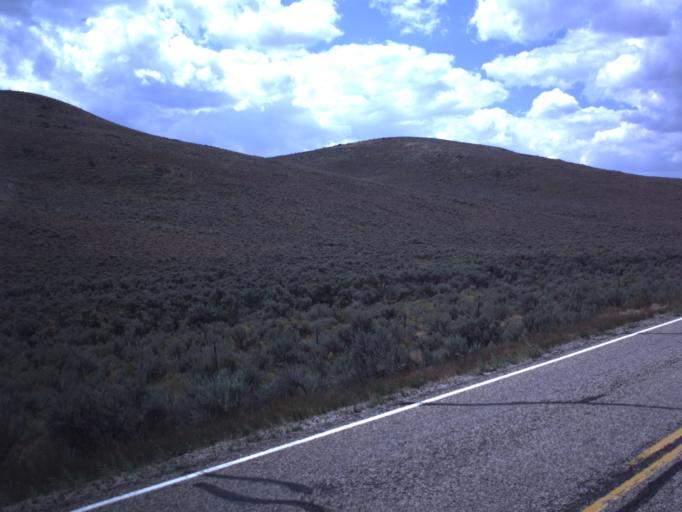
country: US
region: Utah
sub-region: Rich County
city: Randolph
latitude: 41.7683
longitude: -111.1675
